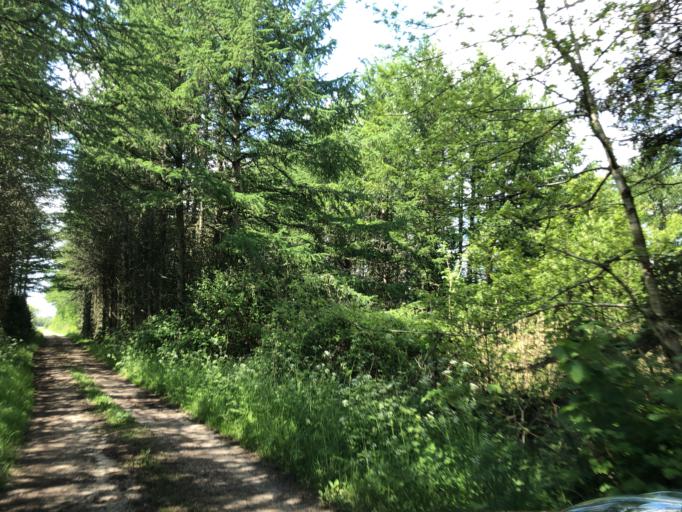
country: DK
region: Central Jutland
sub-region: Holstebro Kommune
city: Ulfborg
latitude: 56.2414
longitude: 8.4278
